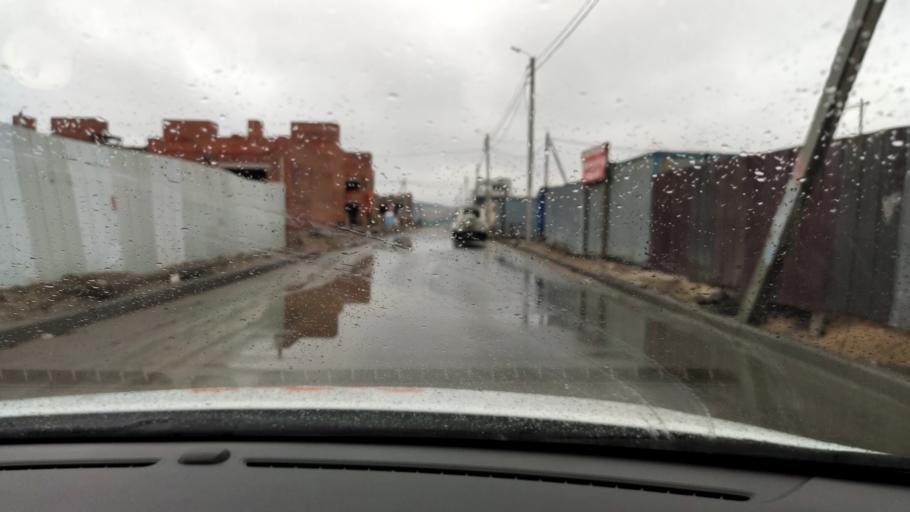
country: RU
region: Tatarstan
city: Staroye Arakchino
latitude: 55.7997
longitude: 48.9622
